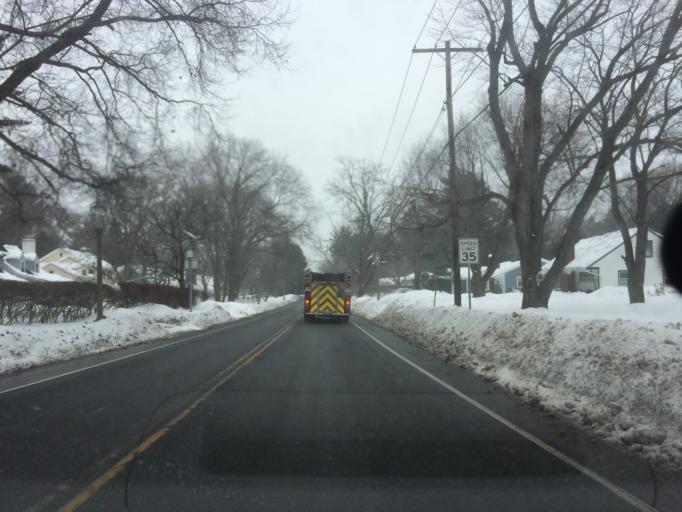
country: US
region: New York
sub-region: Monroe County
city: Brighton
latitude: 43.1269
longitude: -77.5496
